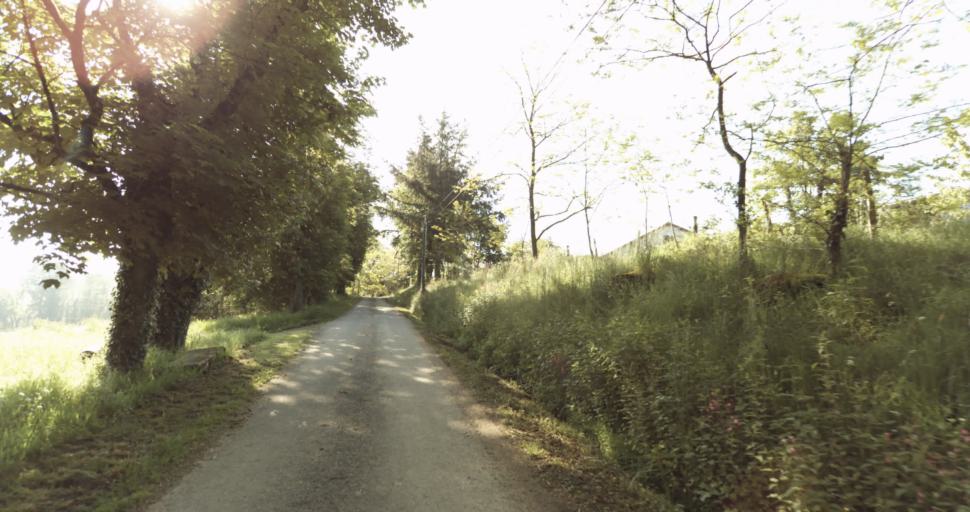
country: FR
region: Limousin
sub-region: Departement de la Haute-Vienne
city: Le Vigen
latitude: 45.7460
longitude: 1.3013
